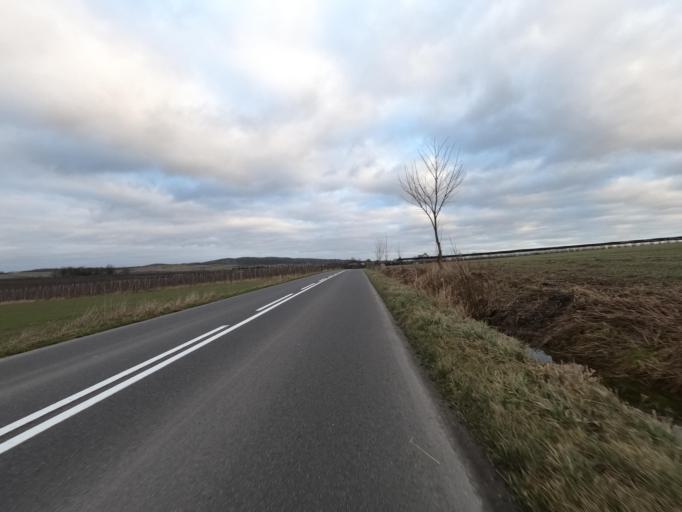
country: PL
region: Greater Poland Voivodeship
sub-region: Powiat pilski
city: Bialosliwie
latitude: 53.1104
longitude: 17.1662
